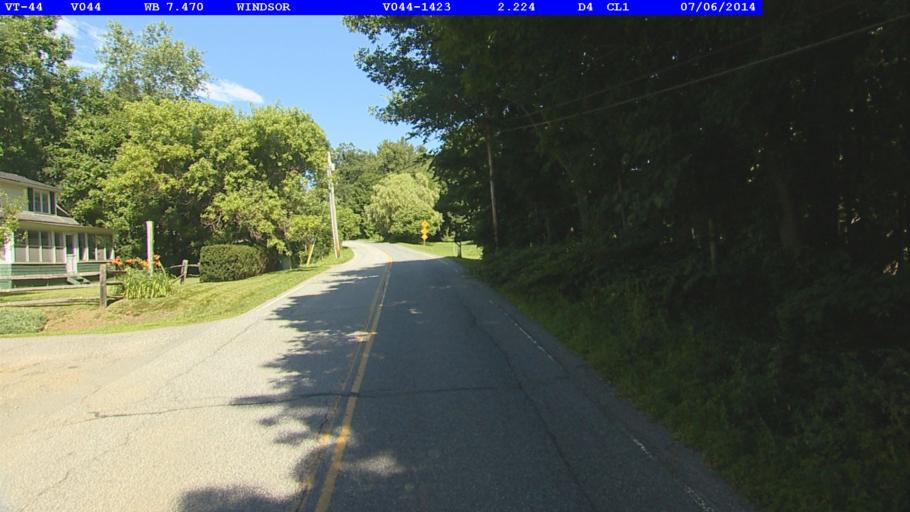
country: US
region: Vermont
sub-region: Windsor County
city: Windsor
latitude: 43.4559
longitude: -72.4130
